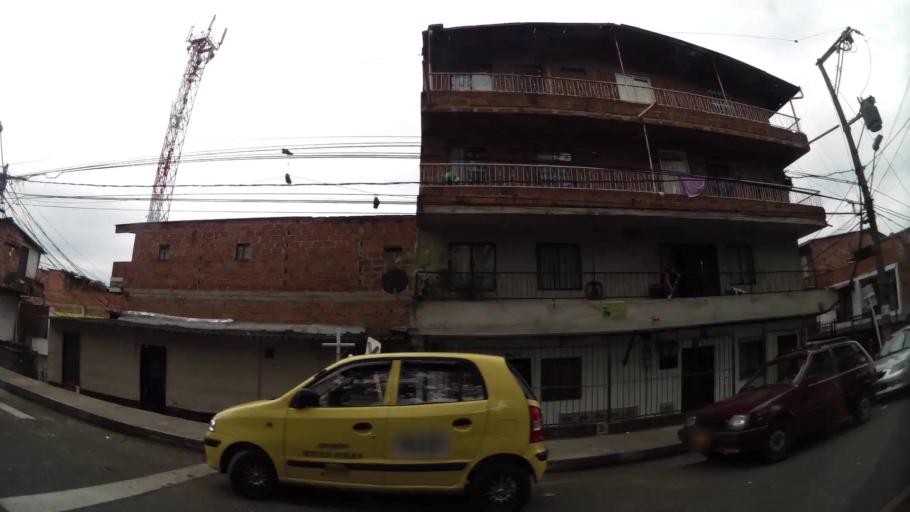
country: CO
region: Antioquia
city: Bello
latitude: 6.2954
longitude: -75.5543
